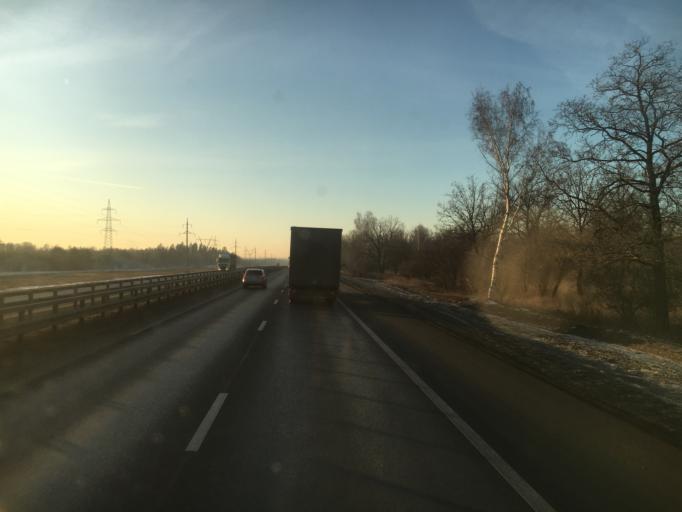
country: RU
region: Samara
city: Pribrezhnyy
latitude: 53.5182
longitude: 49.7996
